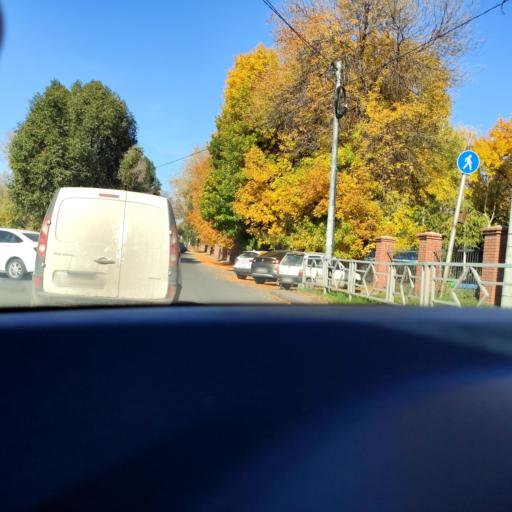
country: RU
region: Samara
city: Petra-Dubrava
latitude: 53.2340
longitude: 50.2658
